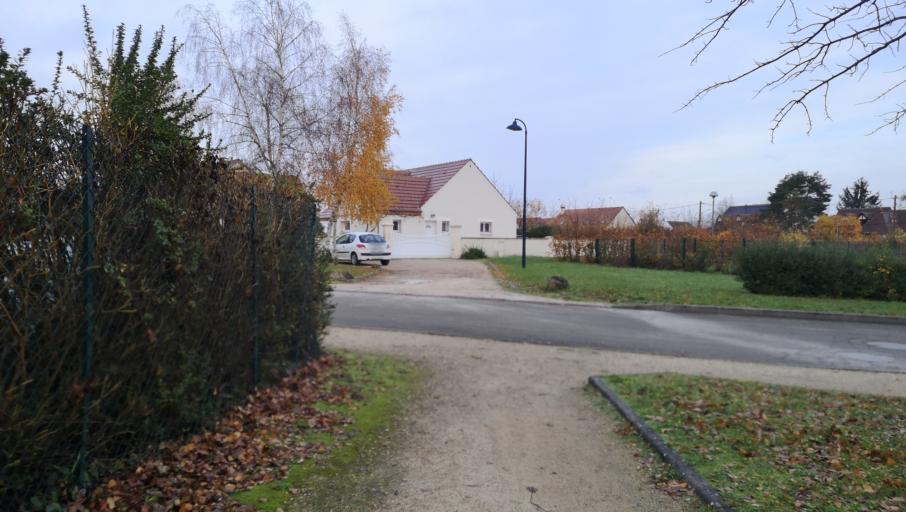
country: FR
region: Centre
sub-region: Departement du Loiret
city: Semoy
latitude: 47.9354
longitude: 1.9471
